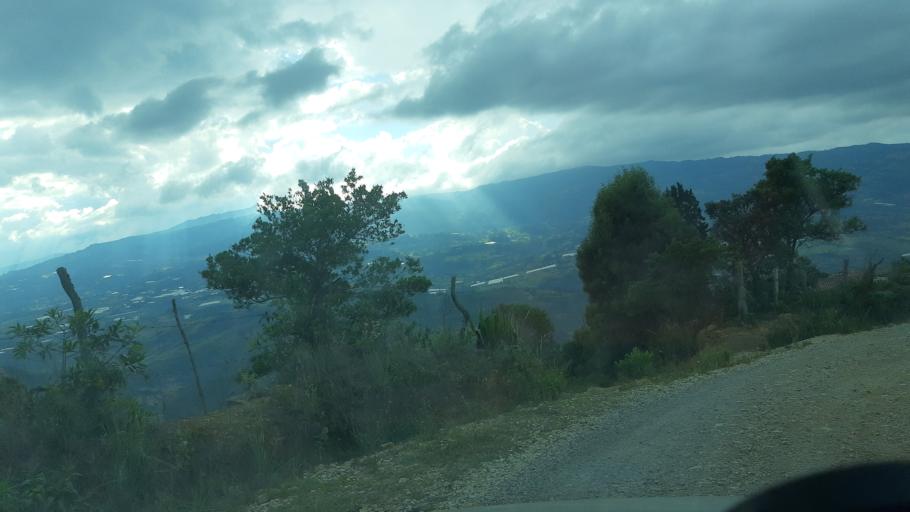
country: CO
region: Boyaca
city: Santa Sofia
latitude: 5.7446
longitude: -73.5625
